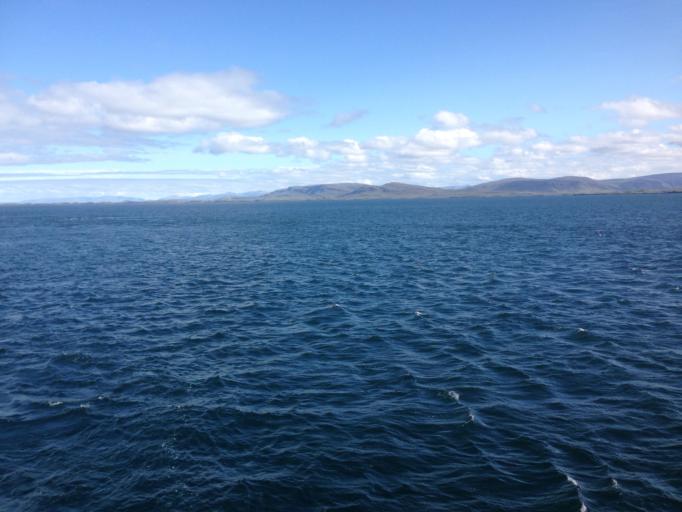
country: IS
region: West
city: Stykkisholmur
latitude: 65.0809
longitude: -22.6696
